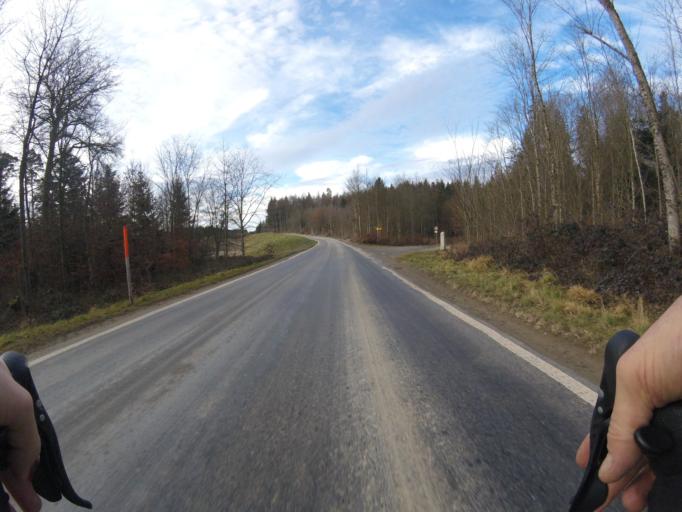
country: CH
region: Fribourg
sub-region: Sense District
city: Flamatt
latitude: 46.9138
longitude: 7.3390
